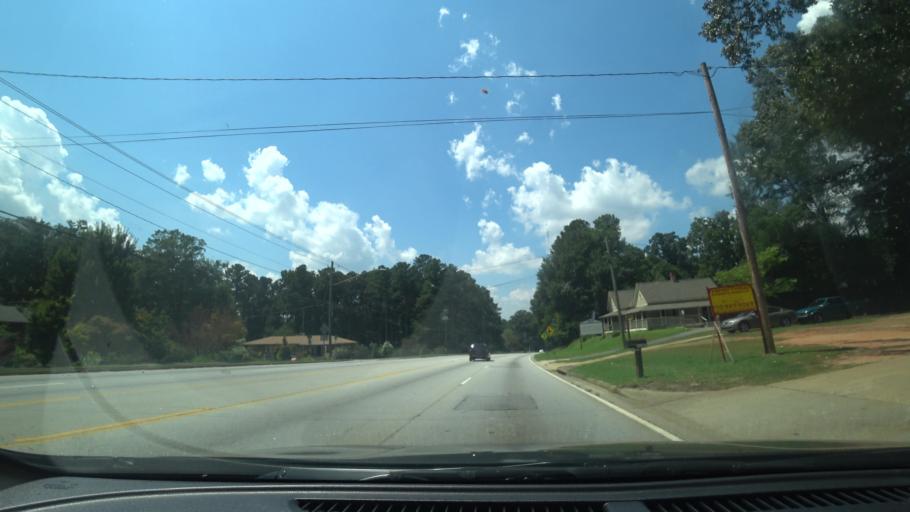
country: US
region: Georgia
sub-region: DeKalb County
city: Redan
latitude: 33.7239
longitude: -84.1764
